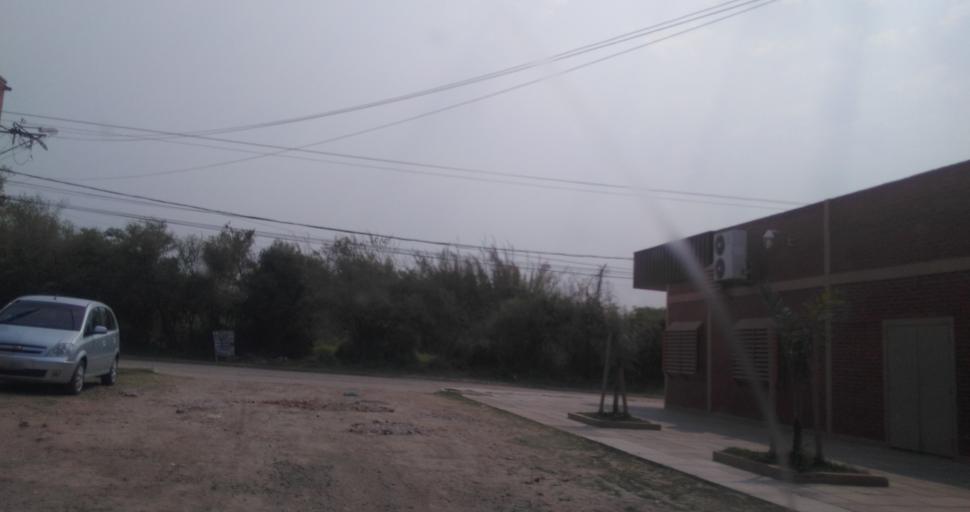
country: AR
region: Chaco
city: Fontana
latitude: -27.4282
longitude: -59.0338
